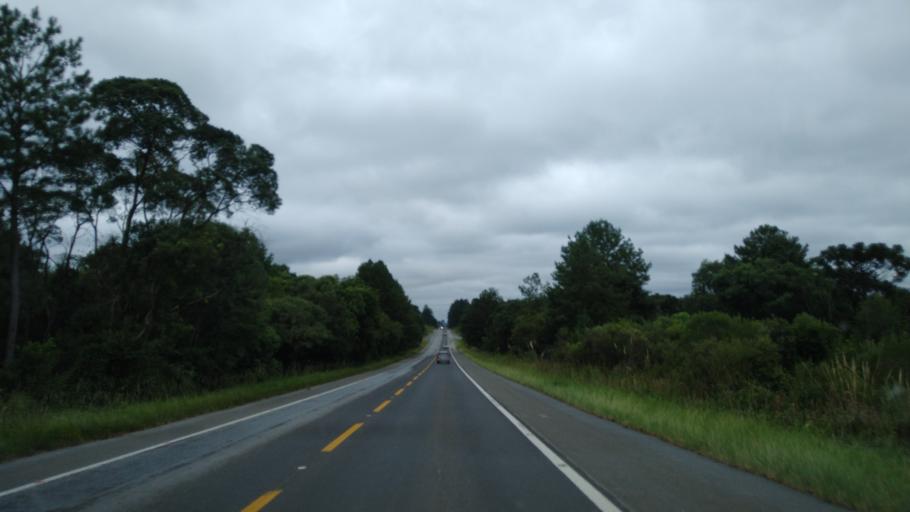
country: BR
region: Santa Catarina
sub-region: Tres Barras
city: Tres Barras
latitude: -26.1728
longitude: -50.1631
